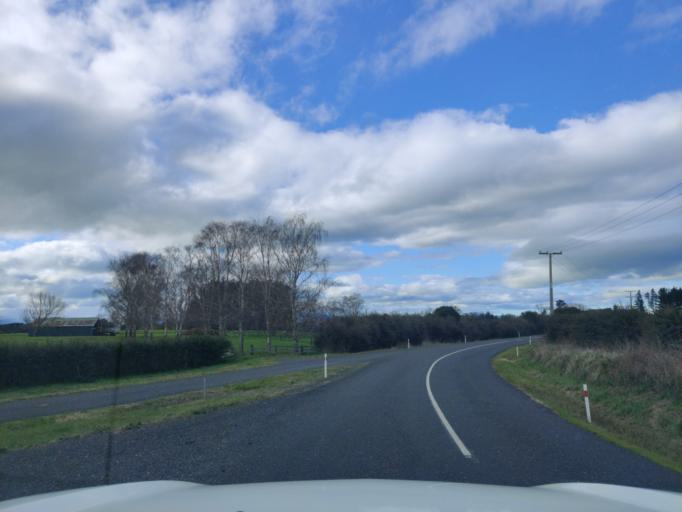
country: NZ
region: Waikato
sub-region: Hauraki District
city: Paeroa
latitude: -37.5895
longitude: 175.5185
